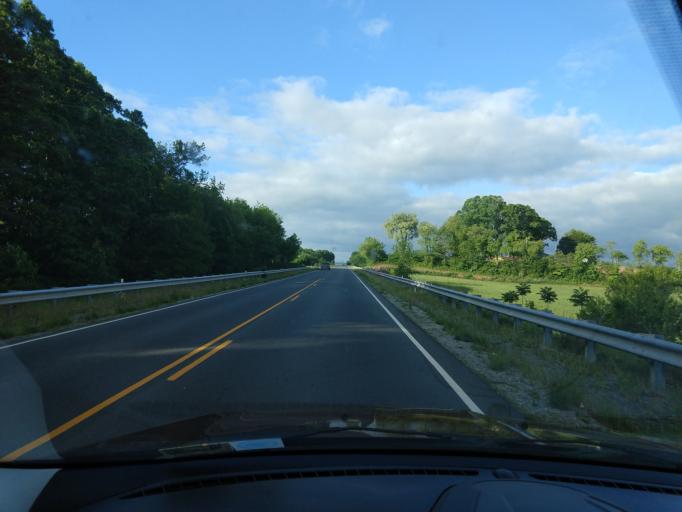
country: US
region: Virginia
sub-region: Wythe County
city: Wytheville
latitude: 36.8767
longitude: -80.9828
